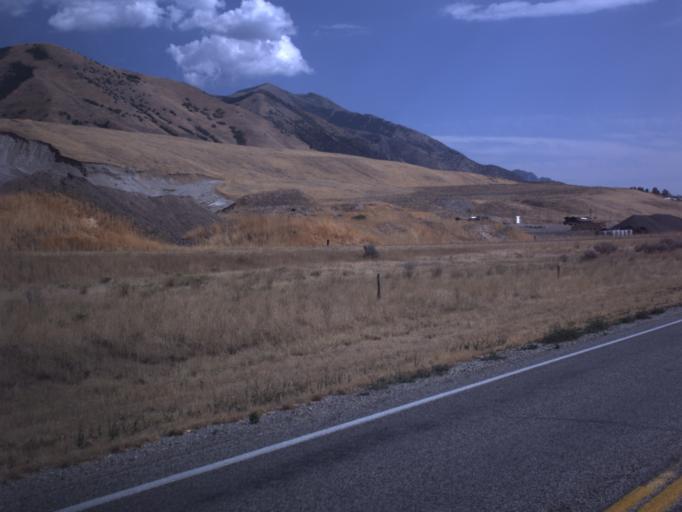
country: US
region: Utah
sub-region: Box Elder County
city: Garland
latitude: 41.7474
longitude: -112.0994
